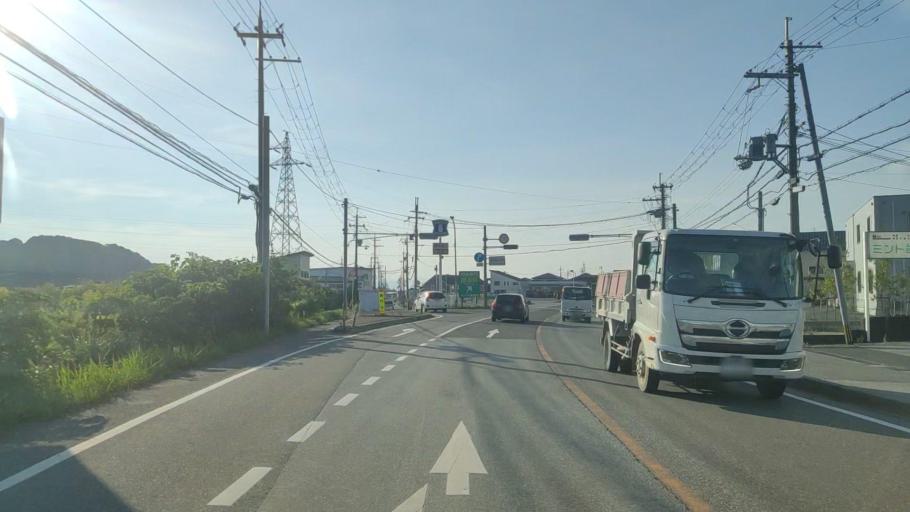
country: JP
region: Shiga Prefecture
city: Hikone
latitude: 35.2455
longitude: 136.2772
